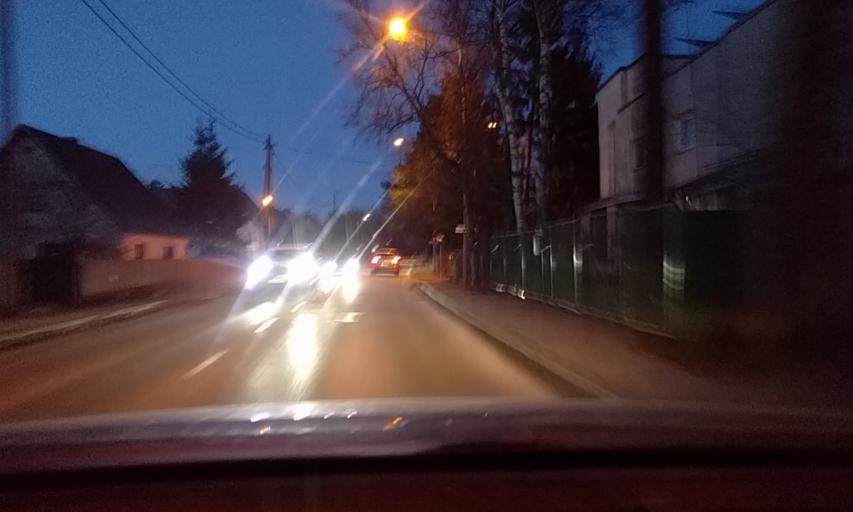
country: EE
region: Harju
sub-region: Viimsi vald
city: Viimsi
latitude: 59.4824
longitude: 24.8587
